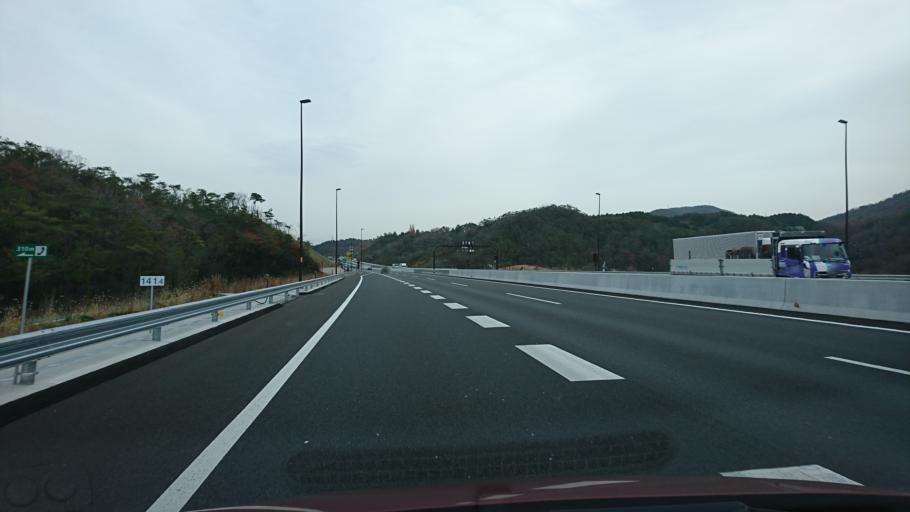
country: JP
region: Hyogo
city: Sandacho
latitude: 34.8663
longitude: 135.3073
